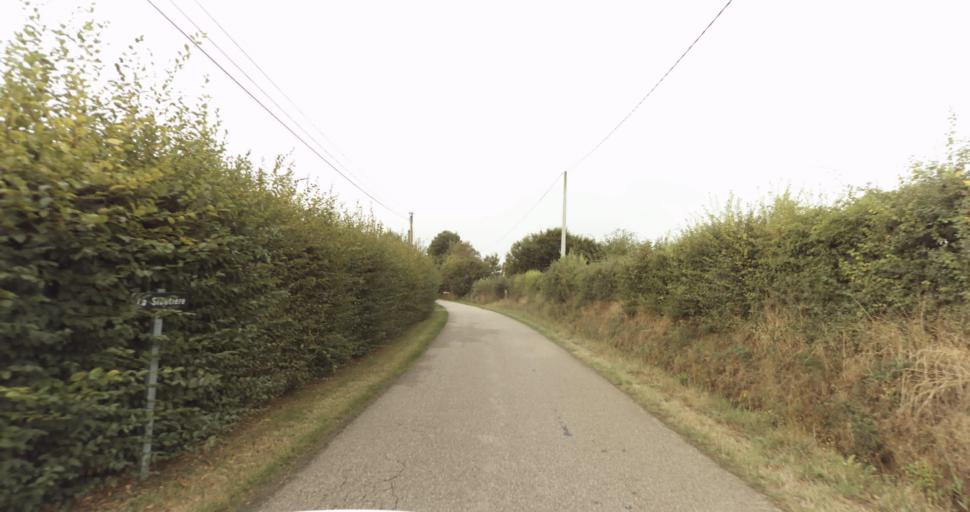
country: FR
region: Lower Normandy
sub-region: Departement du Calvados
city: Livarot
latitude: 48.9241
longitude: 0.1061
